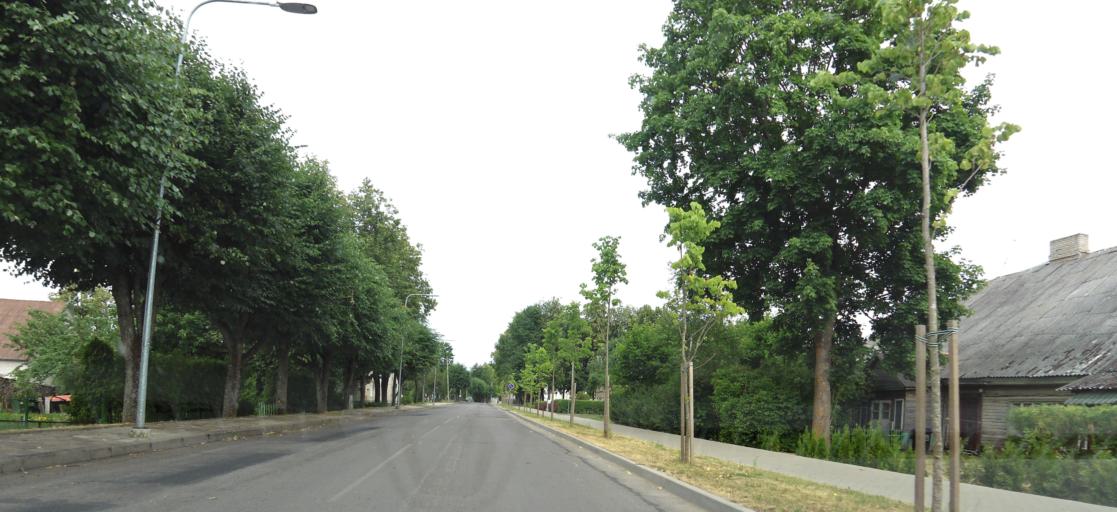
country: LT
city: Sirvintos
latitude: 55.0362
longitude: 24.9685
